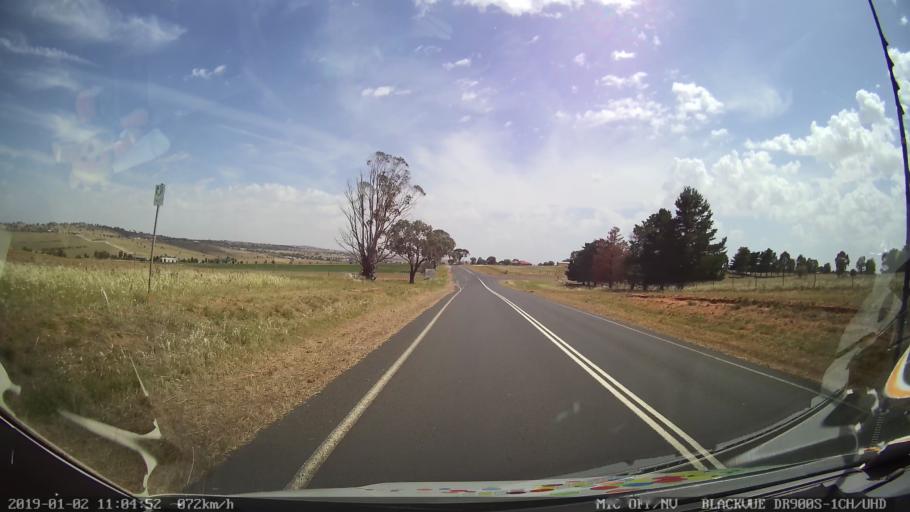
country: AU
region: New South Wales
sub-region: Young
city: Young
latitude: -34.5716
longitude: 148.3539
